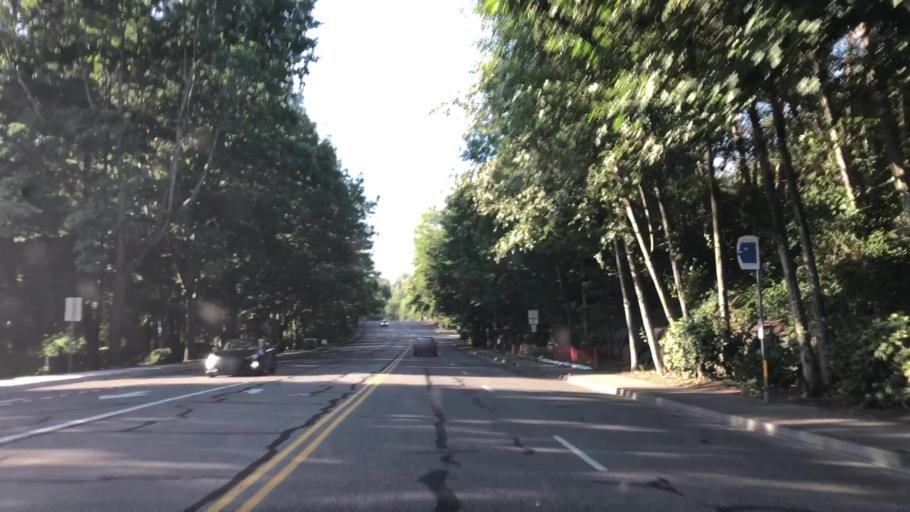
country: US
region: Washington
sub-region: King County
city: Woodinville
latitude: 47.7749
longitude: -122.1802
